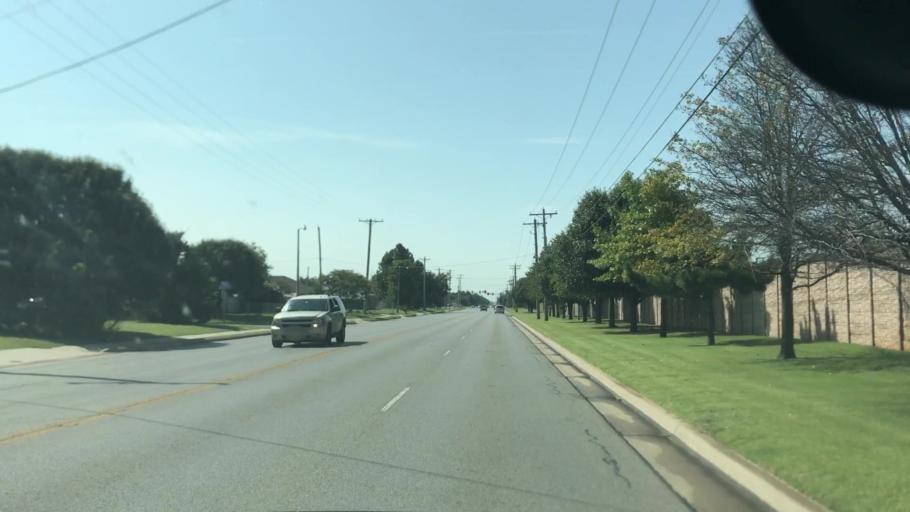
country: US
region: Oklahoma
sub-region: Cleveland County
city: Moore
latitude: 35.3526
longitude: -97.5122
